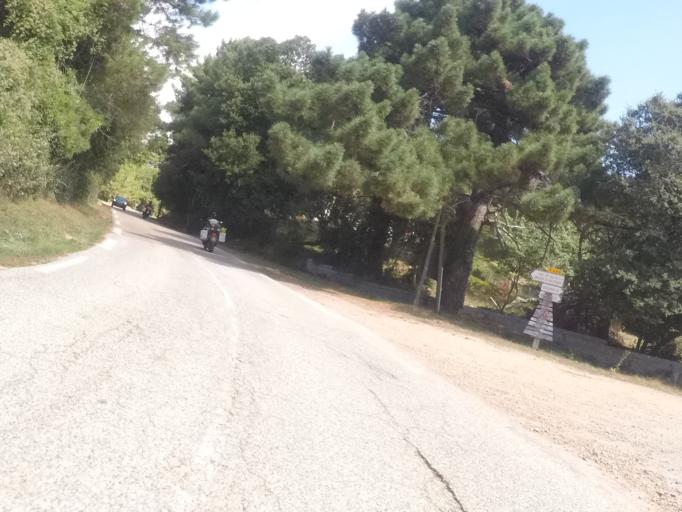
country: FR
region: Corsica
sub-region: Departement de la Corse-du-Sud
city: Zonza
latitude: 41.7600
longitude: 9.1883
